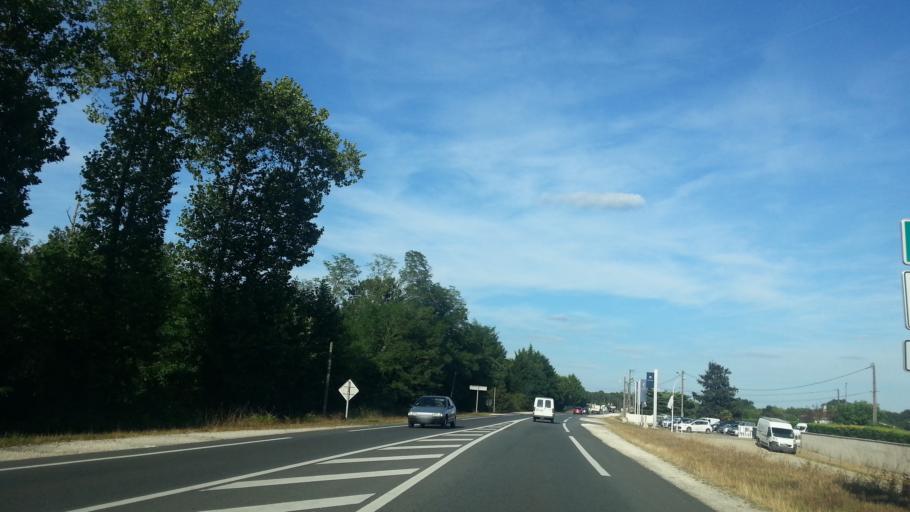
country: FR
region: Aquitaine
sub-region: Departement de la Gironde
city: Ayguemorte-les-Graves
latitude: 44.6950
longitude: -0.4918
